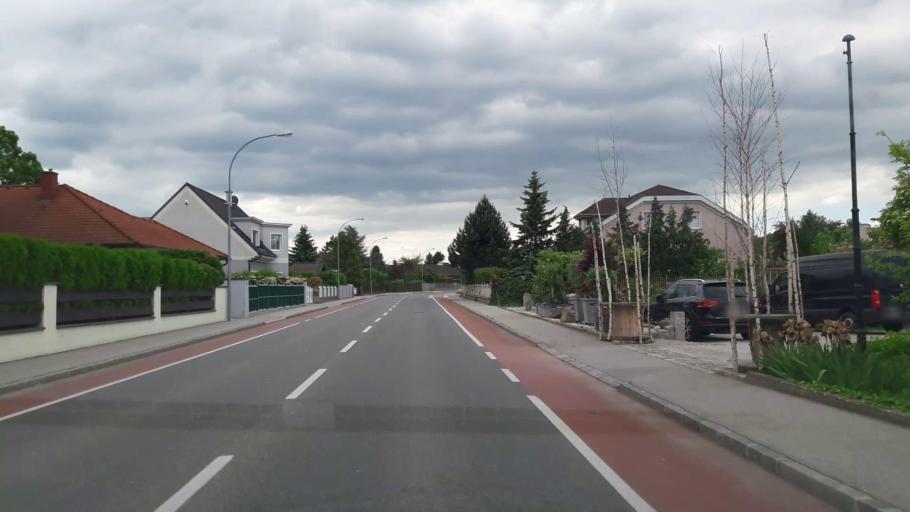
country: AT
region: Lower Austria
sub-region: Wiener Neustadt Stadt
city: Wiener Neustadt
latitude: 47.8102
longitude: 16.2600
